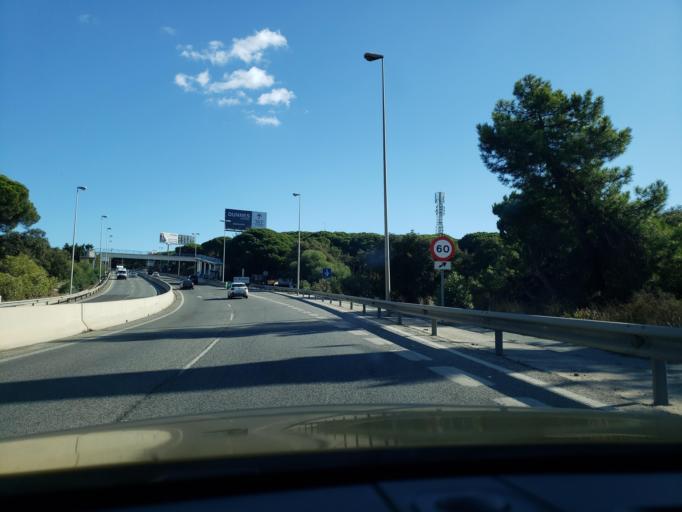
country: ES
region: Andalusia
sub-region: Provincia de Malaga
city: Ojen
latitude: 36.4932
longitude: -4.7625
